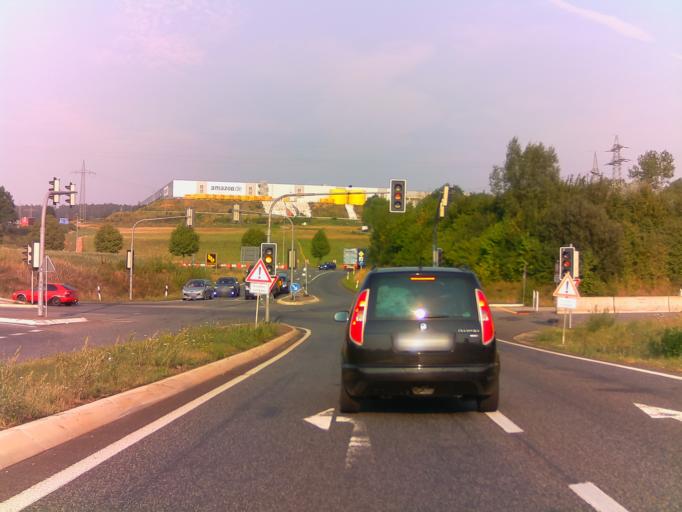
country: DE
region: Hesse
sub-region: Regierungsbezirk Kassel
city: Bad Hersfeld
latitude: 50.8524
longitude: 9.7216
